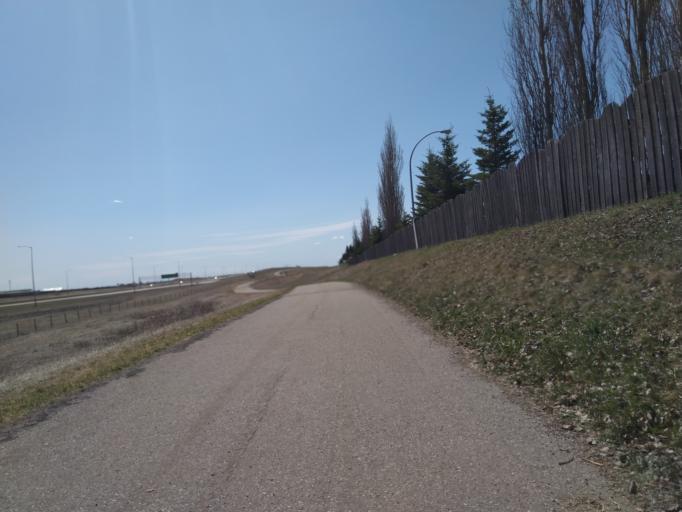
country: CA
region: Alberta
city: Chestermere
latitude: 51.0792
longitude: -113.9229
